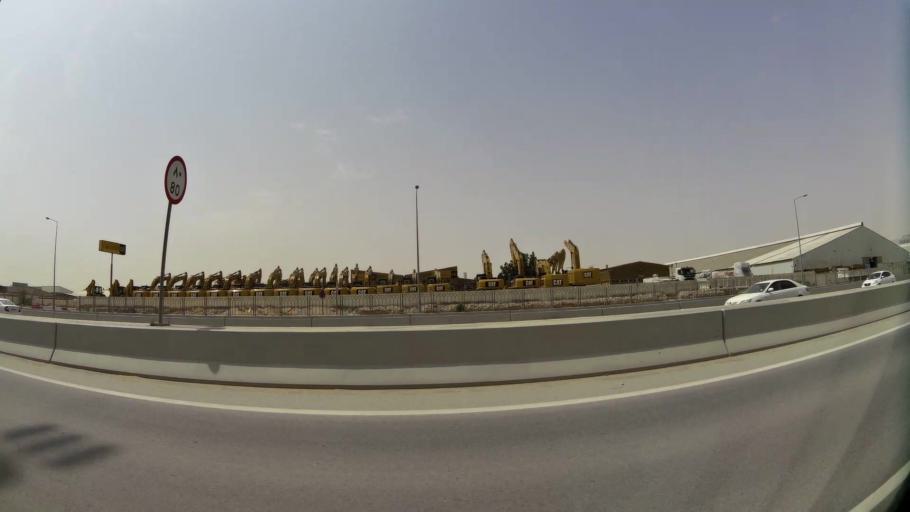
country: QA
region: Baladiyat ar Rayyan
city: Ar Rayyan
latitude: 25.2099
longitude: 51.4429
